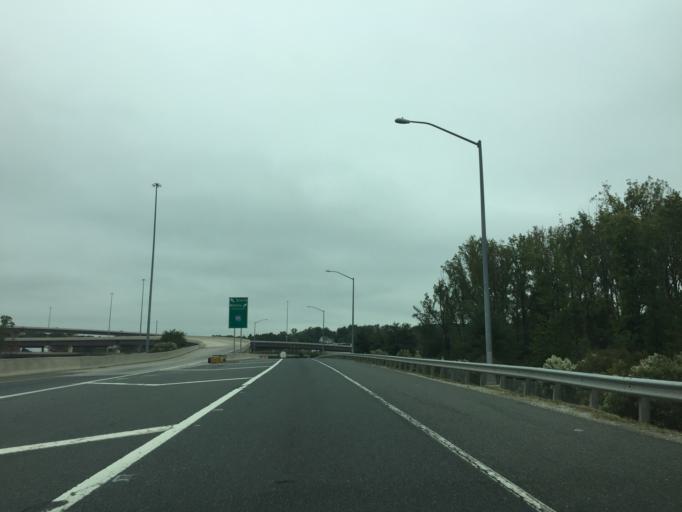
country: US
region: Maryland
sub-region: Baltimore County
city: Rossville
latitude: 39.3473
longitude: -76.4935
